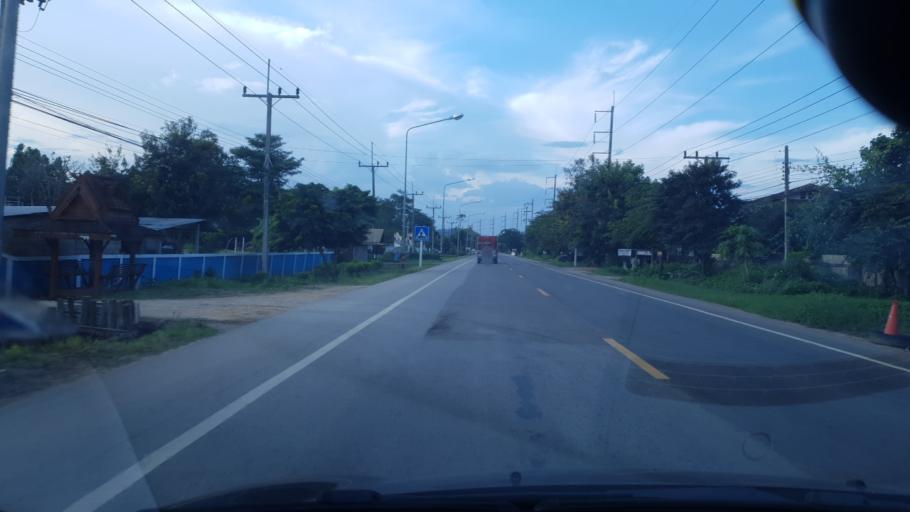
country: TH
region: Chiang Rai
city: Wiang Pa Pao
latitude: 19.4860
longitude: 99.4792
